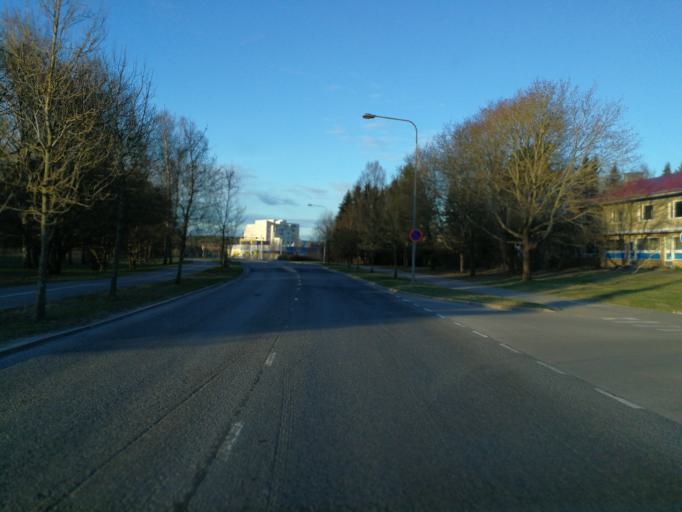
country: FI
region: Varsinais-Suomi
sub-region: Turku
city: Turku
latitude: 60.4320
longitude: 22.2403
